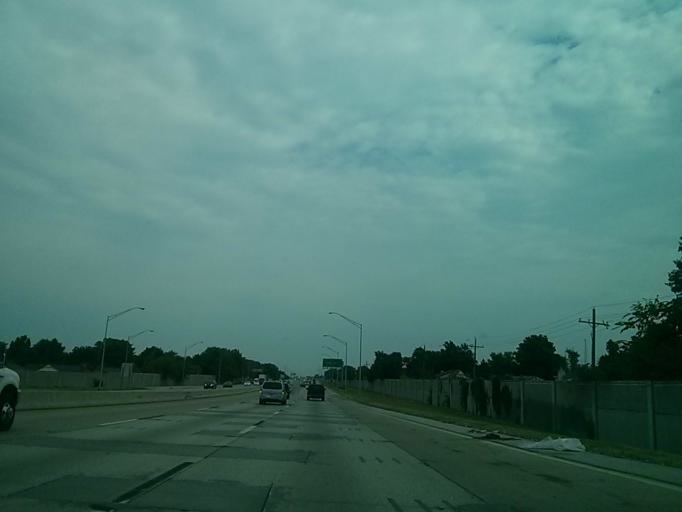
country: US
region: Oklahoma
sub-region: Tulsa County
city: Broken Arrow
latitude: 36.1205
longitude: -95.8596
